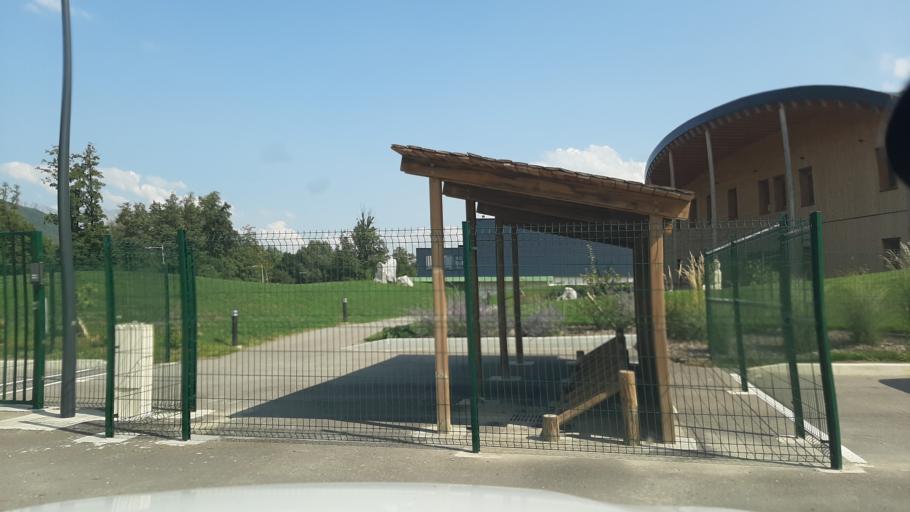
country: FR
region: Rhone-Alpes
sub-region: Departement de la Savoie
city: La Rochette
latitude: 45.4693
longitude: 6.1282
